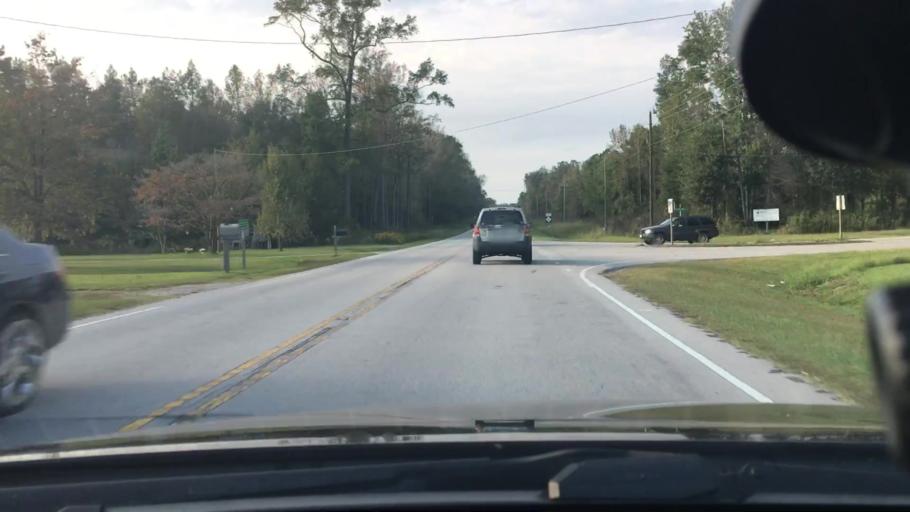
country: US
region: North Carolina
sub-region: Pitt County
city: Windsor
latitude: 35.4867
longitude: -77.3036
